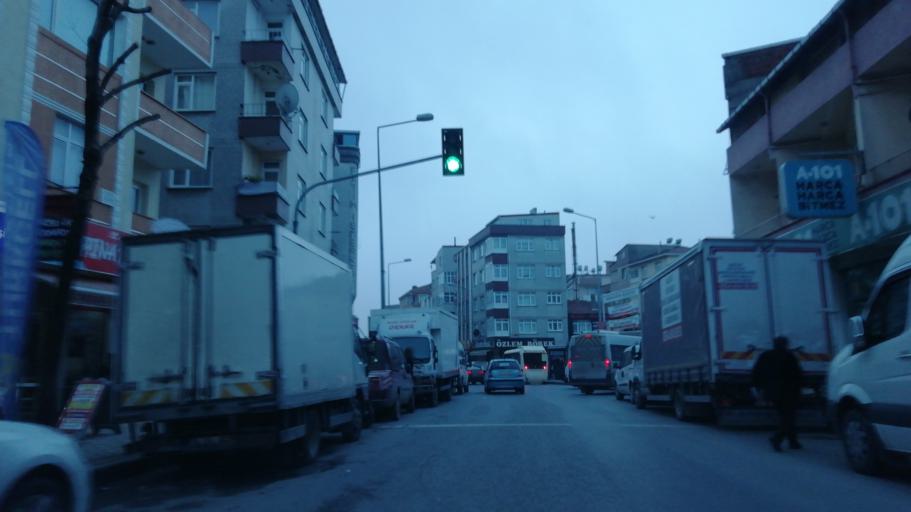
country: TR
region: Istanbul
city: Bahcelievler
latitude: 41.0085
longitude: 28.8310
